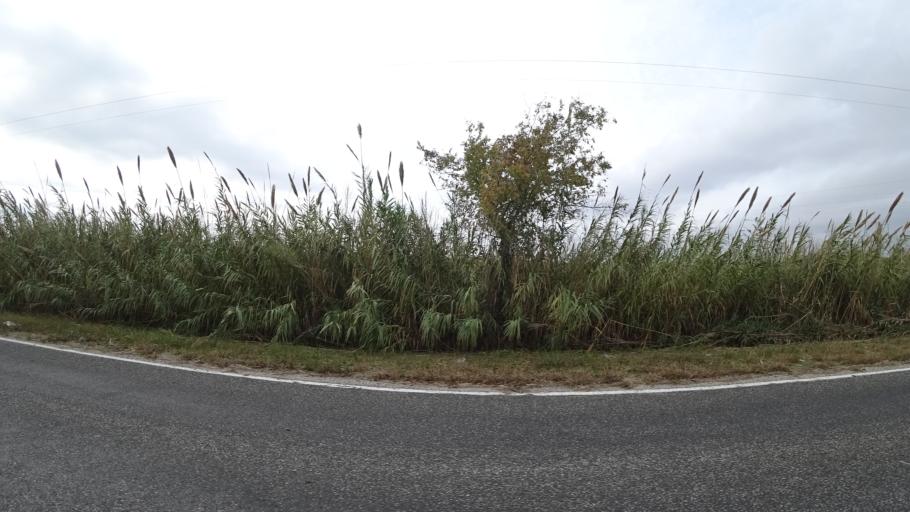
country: US
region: Texas
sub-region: Travis County
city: Manor
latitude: 30.3750
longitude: -97.5765
